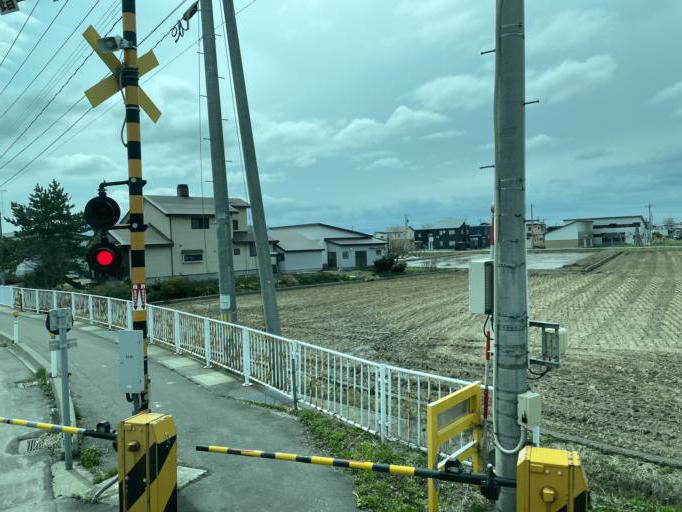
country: JP
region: Aomori
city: Goshogawara
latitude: 40.7664
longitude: 140.4348
